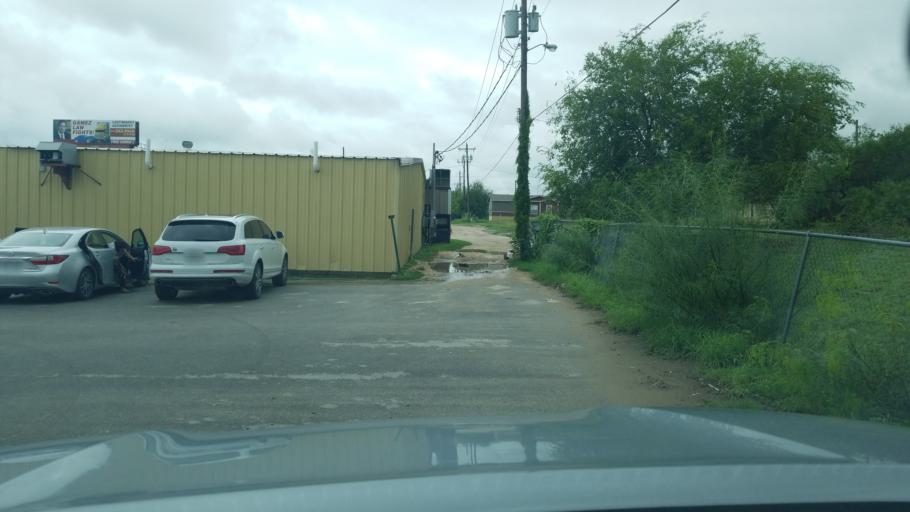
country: US
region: Texas
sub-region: Dimmit County
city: Carrizo Springs
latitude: 28.5255
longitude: -99.8561
